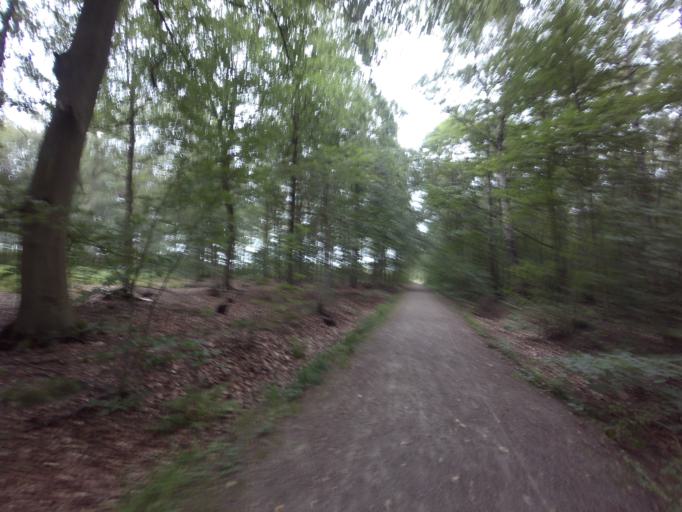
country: SE
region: Skane
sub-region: Helsingborg
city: Helsingborg
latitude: 56.0879
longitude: 12.6822
